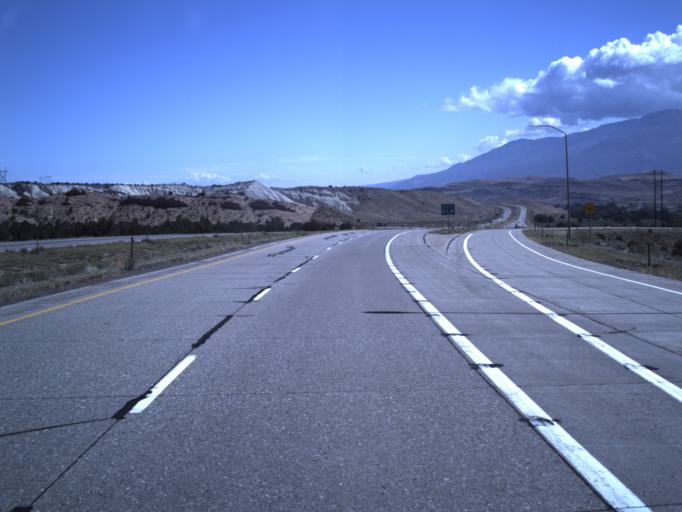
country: US
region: Utah
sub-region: Sevier County
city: Monroe
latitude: 38.5978
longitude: -112.2609
